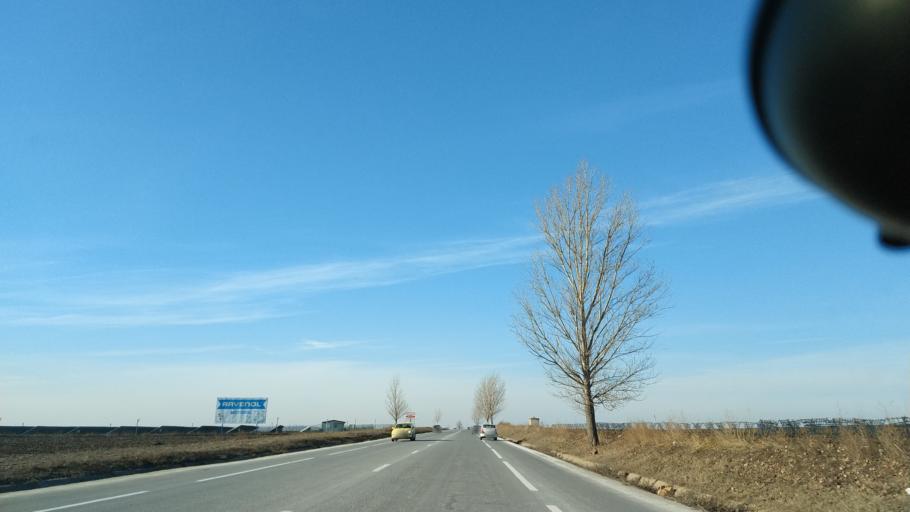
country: RO
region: Iasi
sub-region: Comuna Podu Iloaiei
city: Budai
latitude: 47.2222
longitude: 27.1978
